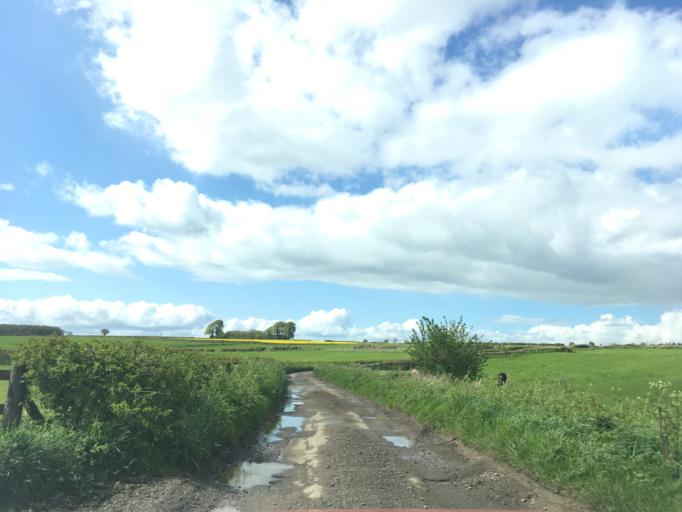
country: GB
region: England
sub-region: Wiltshire
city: Luckington
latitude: 51.5893
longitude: -2.2657
